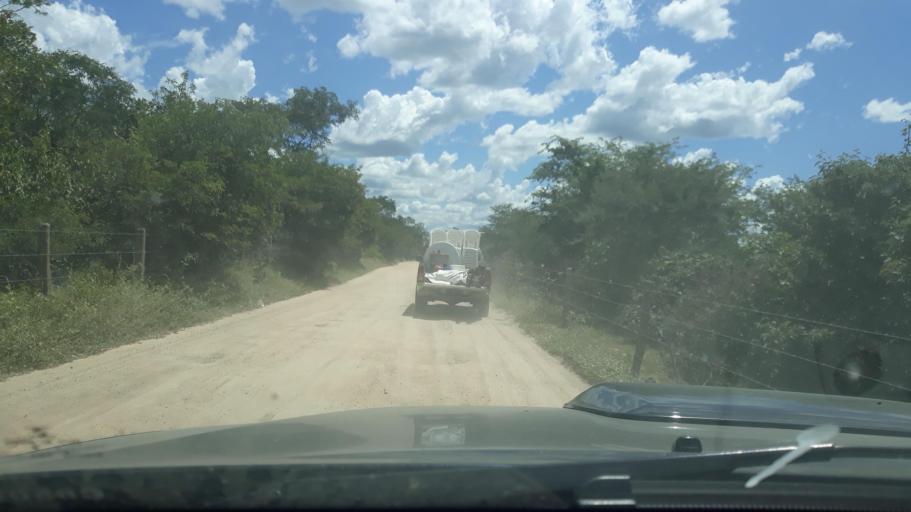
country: BR
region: Bahia
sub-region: Riacho De Santana
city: Riacho de Santana
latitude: -13.9095
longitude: -42.9373
